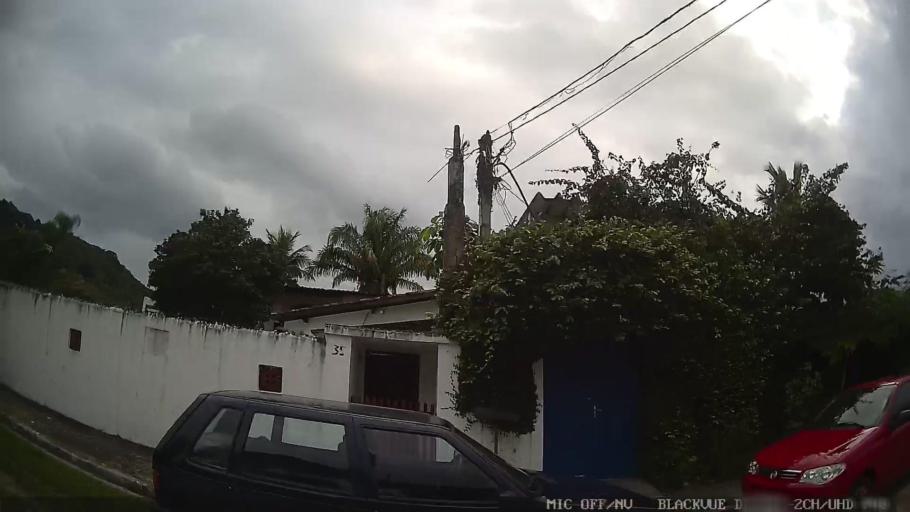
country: BR
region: Sao Paulo
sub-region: Guaruja
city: Guaruja
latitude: -24.0173
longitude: -46.2889
